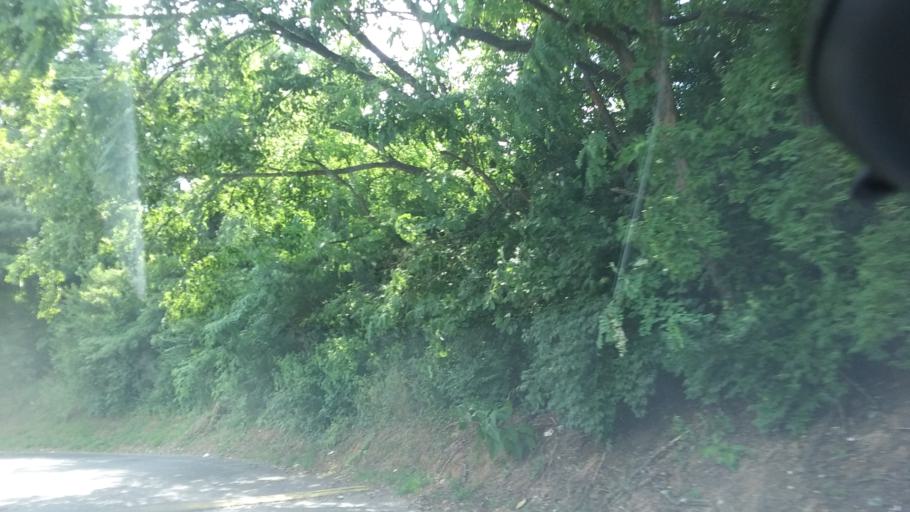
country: US
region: Tennessee
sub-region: Rutherford County
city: La Vergne
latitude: 36.0870
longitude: -86.6506
